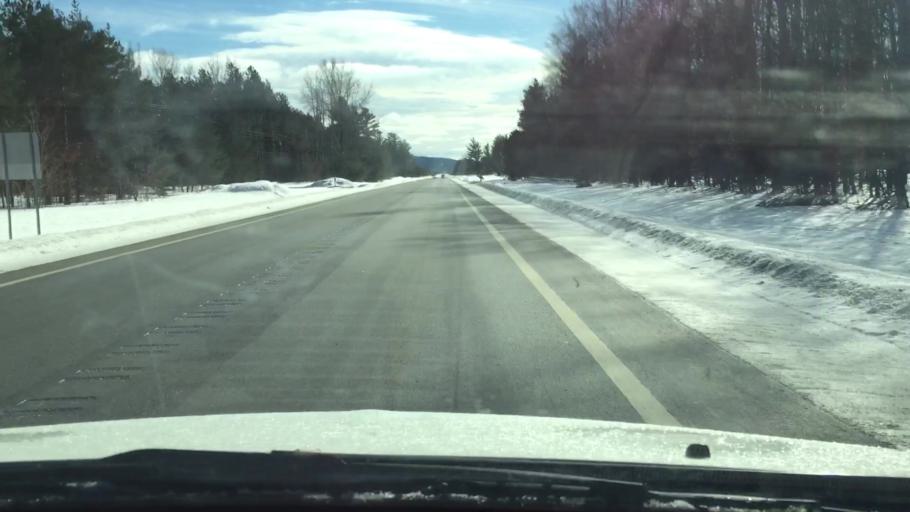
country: US
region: Michigan
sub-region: Antrim County
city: Mancelona
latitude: 44.9380
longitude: -85.0508
